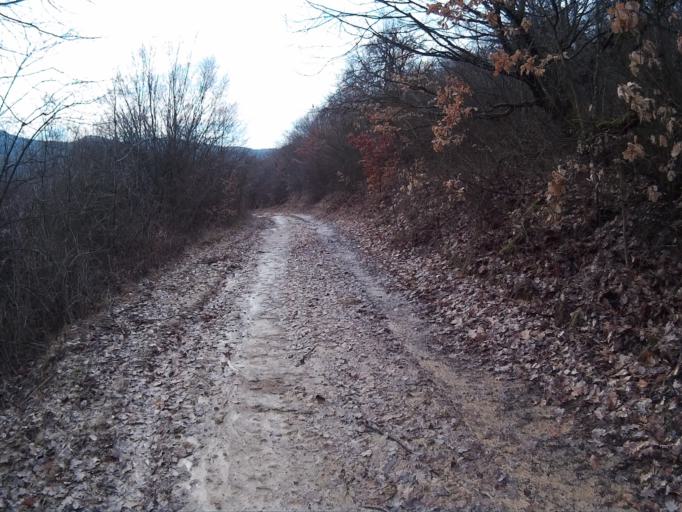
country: HU
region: Borsod-Abauj-Zemplen
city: Satoraljaujhely
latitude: 48.4076
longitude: 21.5998
